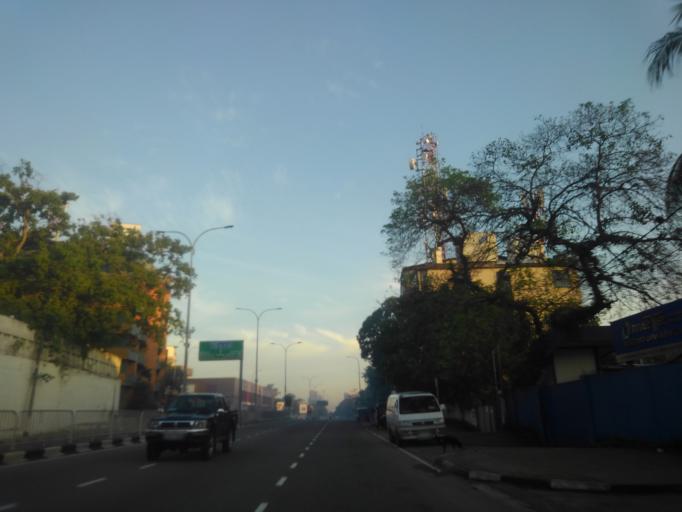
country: LK
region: Western
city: Pita Kotte
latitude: 6.8958
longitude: 79.8771
